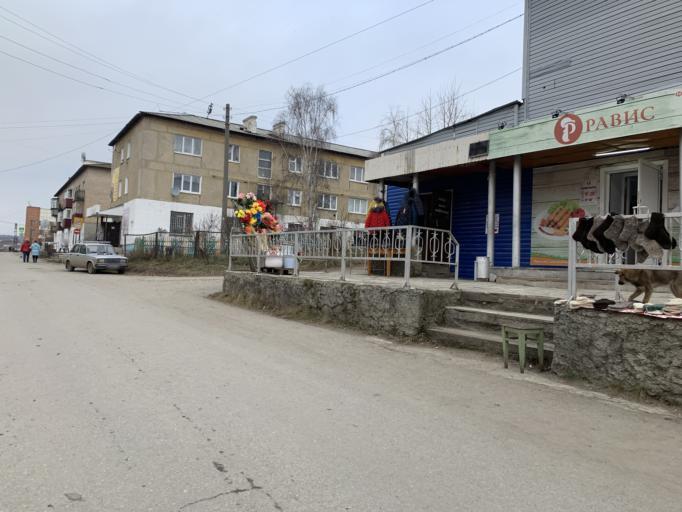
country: RU
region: Chelyabinsk
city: Nyazepetrovsk
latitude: 56.0542
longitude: 59.6001
